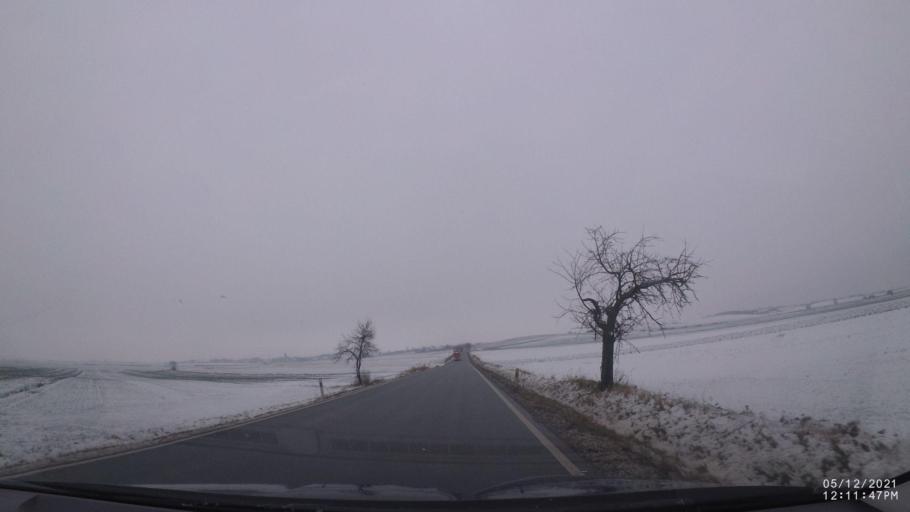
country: CZ
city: Ceske Mezirici
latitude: 50.2891
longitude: 16.0291
